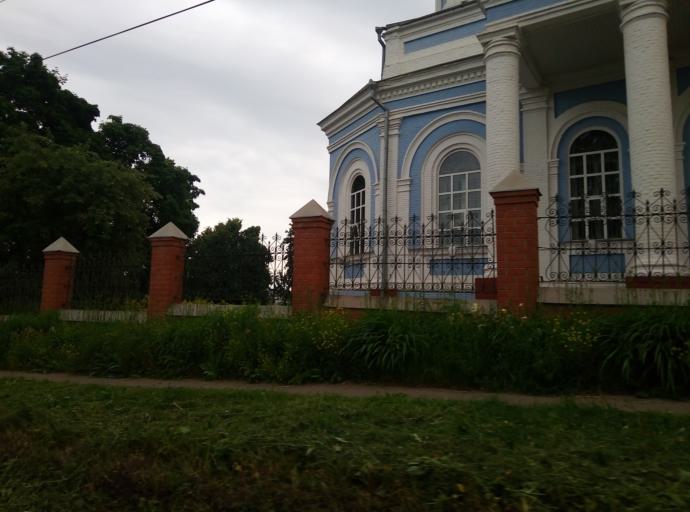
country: RU
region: Kursk
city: Kursk
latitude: 51.7450
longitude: 36.1658
